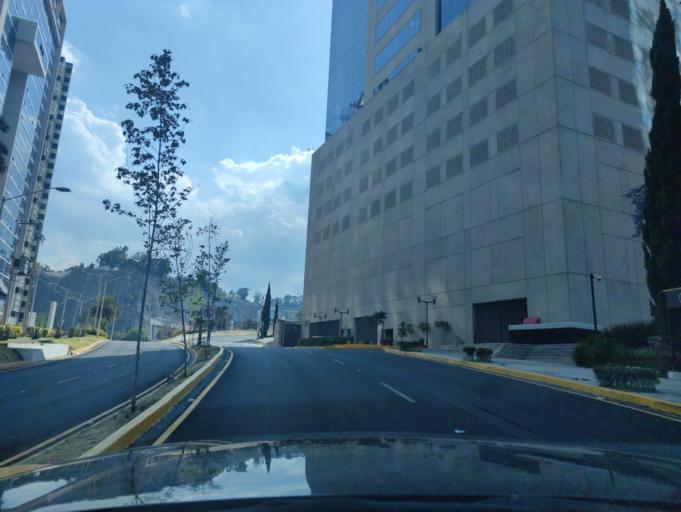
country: MX
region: Mexico City
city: Cuajimalpa
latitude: 19.3571
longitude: -99.2750
